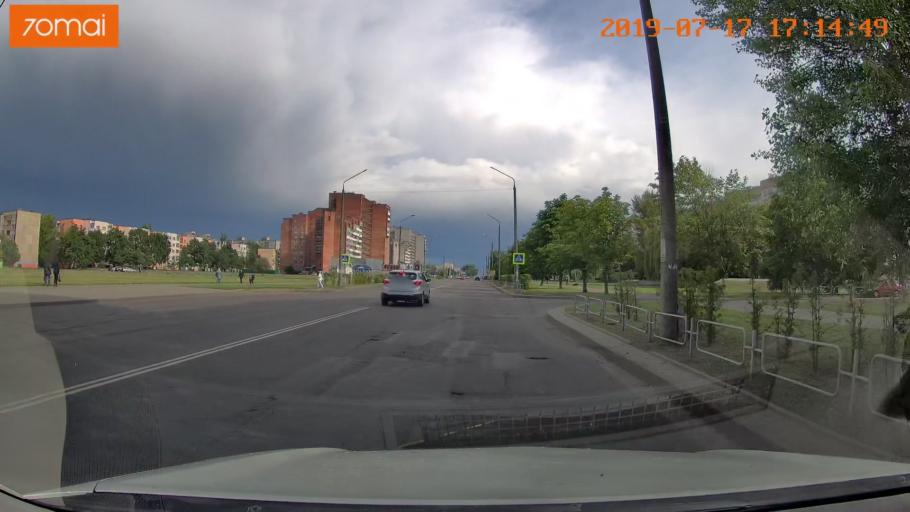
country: BY
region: Mogilev
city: Babruysk
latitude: 53.1734
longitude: 29.1885
